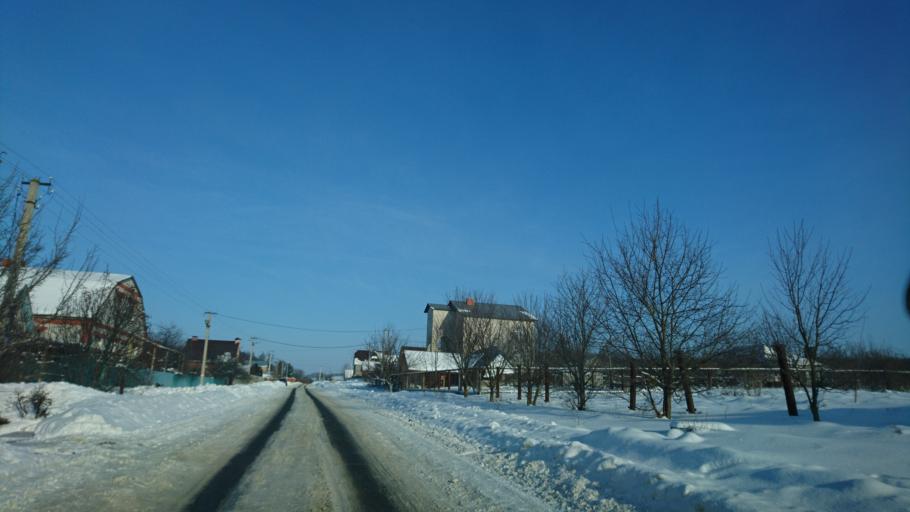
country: RU
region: Belgorod
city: Severnyy
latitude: 50.7224
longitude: 36.6102
